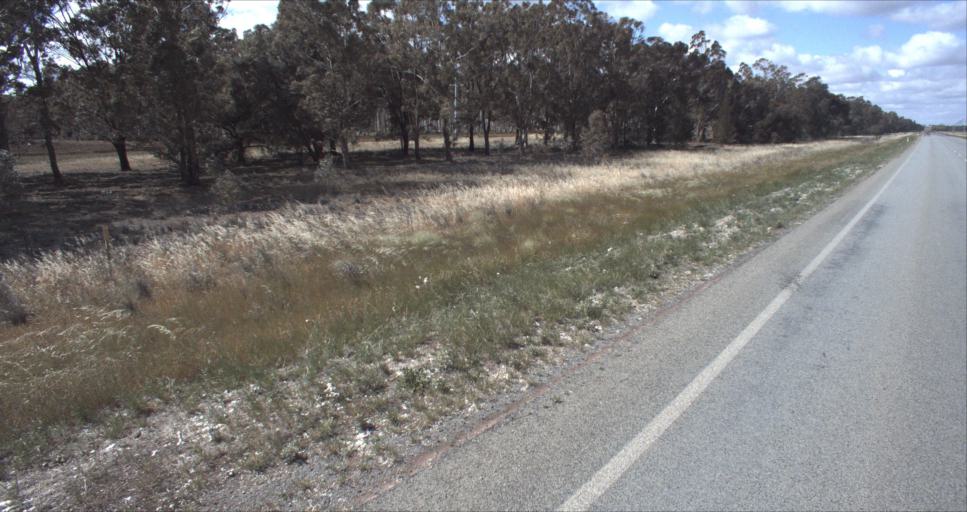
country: AU
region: New South Wales
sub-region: Murrumbidgee Shire
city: Darlington Point
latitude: -34.5807
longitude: 146.1651
